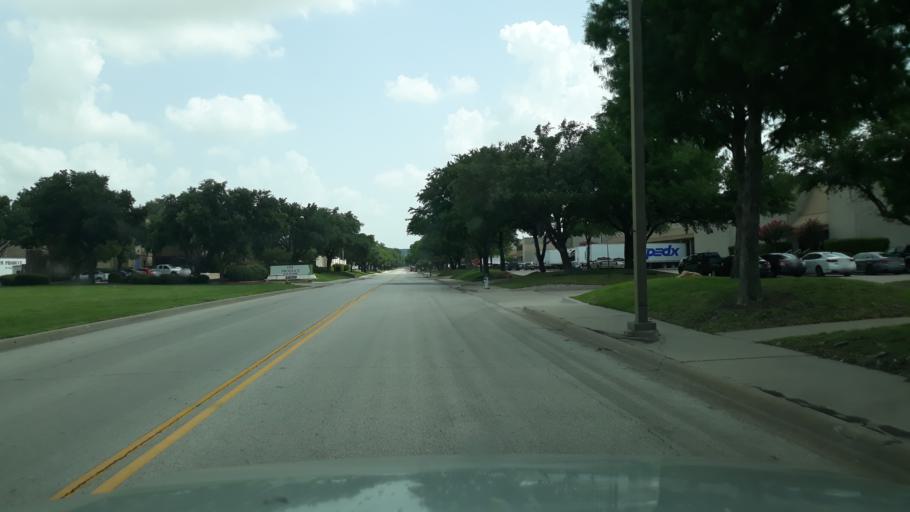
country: US
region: Texas
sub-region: Dallas County
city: Coppell
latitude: 32.9342
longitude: -97.0171
